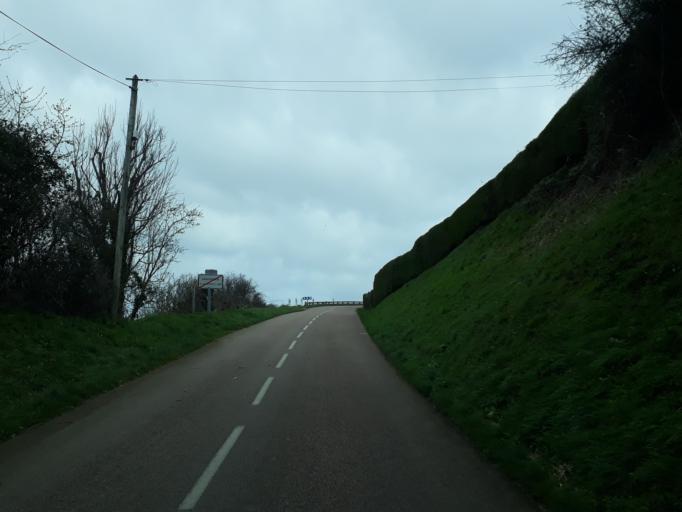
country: FR
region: Haute-Normandie
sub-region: Departement de la Seine-Maritime
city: Yport
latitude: 49.7375
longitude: 0.2934
